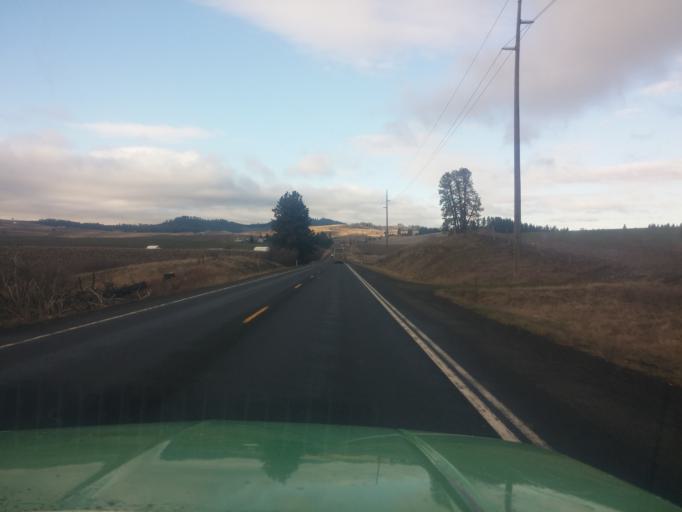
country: US
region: Idaho
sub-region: Latah County
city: Moscow
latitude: 46.9059
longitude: -116.9679
